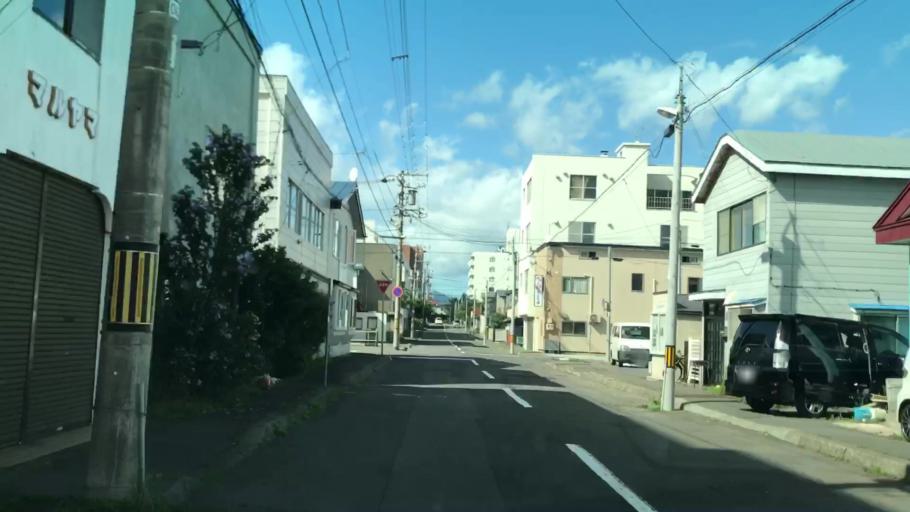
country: JP
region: Hokkaido
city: Muroran
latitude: 42.3133
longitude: 140.9713
